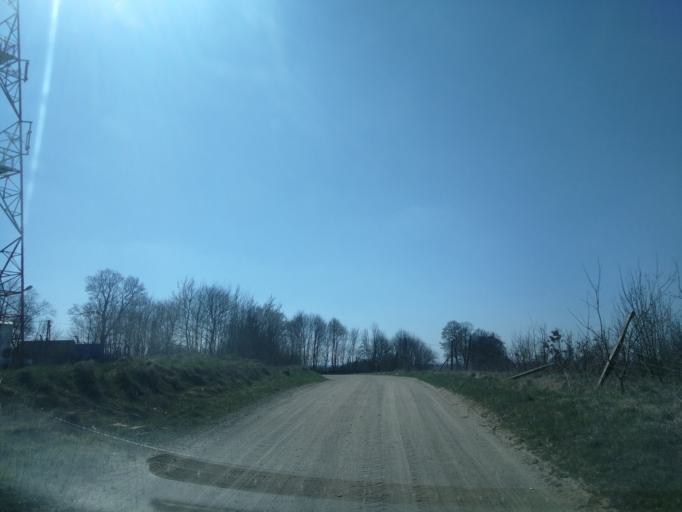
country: PL
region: Warmian-Masurian Voivodeship
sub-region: Powiat ostrodzki
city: Dabrowno
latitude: 53.4389
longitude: 19.9804
